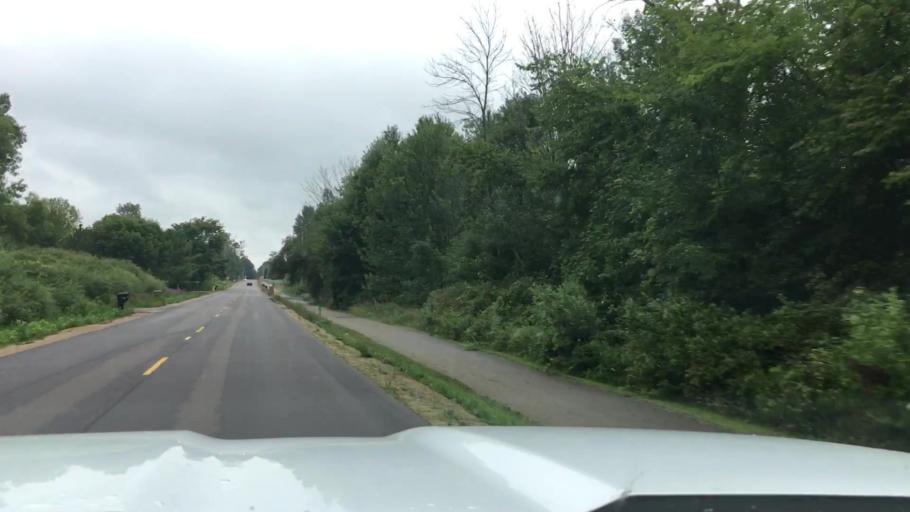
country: US
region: Michigan
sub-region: Ottawa County
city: Jenison
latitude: 42.8407
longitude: -85.7957
